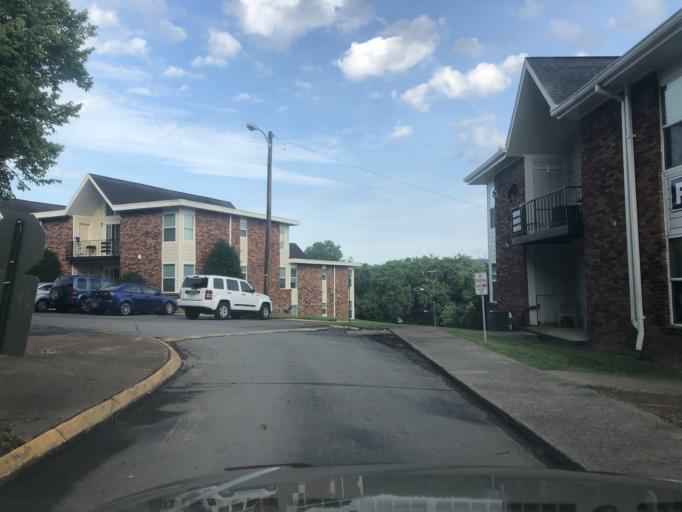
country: US
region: Tennessee
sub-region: Davidson County
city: Goodlettsville
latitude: 36.2504
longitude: -86.7147
